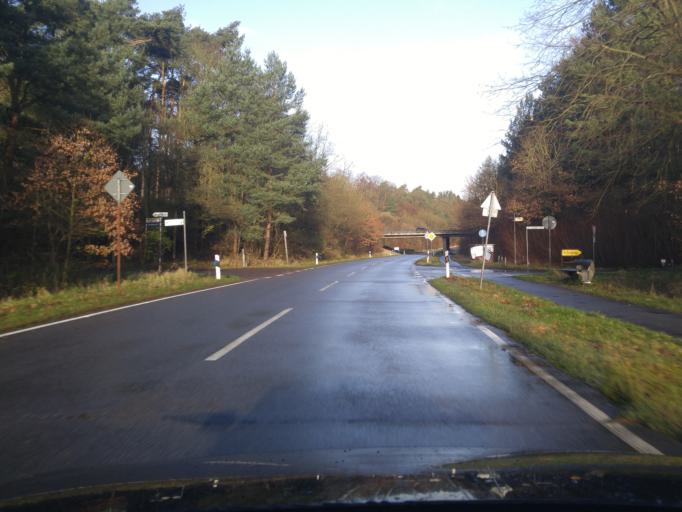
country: DE
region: Schleswig-Holstein
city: Ratekau
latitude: 53.9323
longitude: 10.7351
